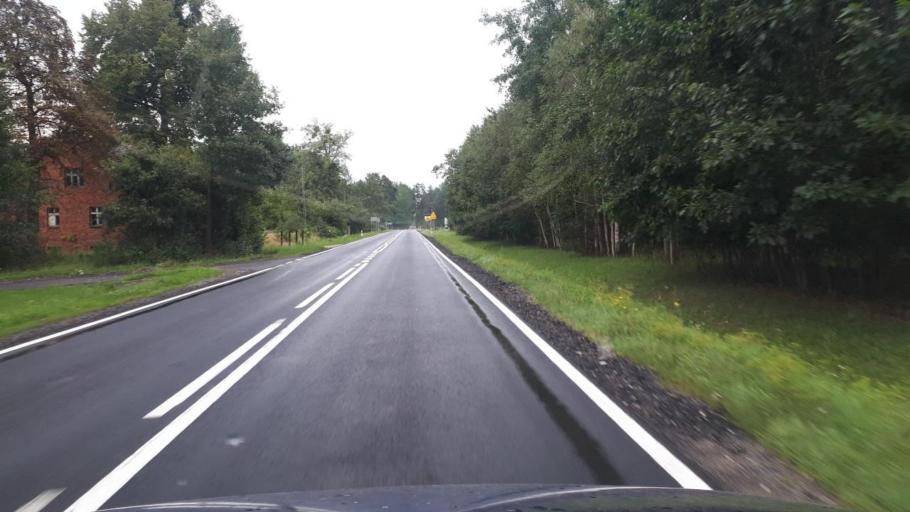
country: PL
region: Silesian Voivodeship
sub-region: Powiat lubliniecki
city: Sierakow Slaski
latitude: 50.8223
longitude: 18.5319
